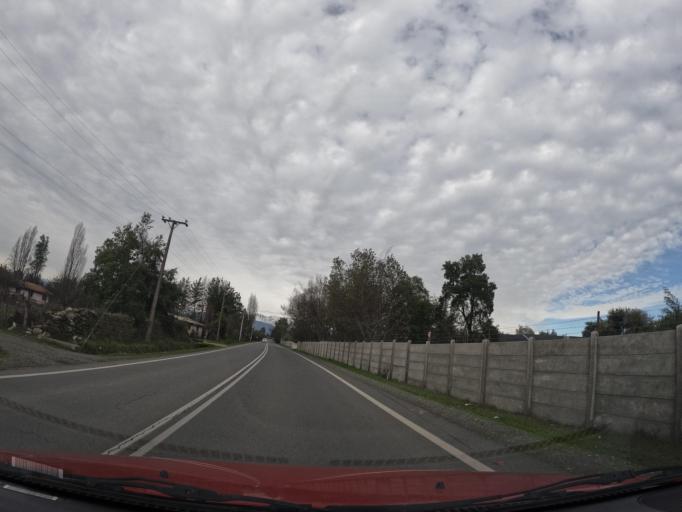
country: CL
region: Maule
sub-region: Provincia de Linares
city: Linares
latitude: -35.9041
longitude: -71.5082
